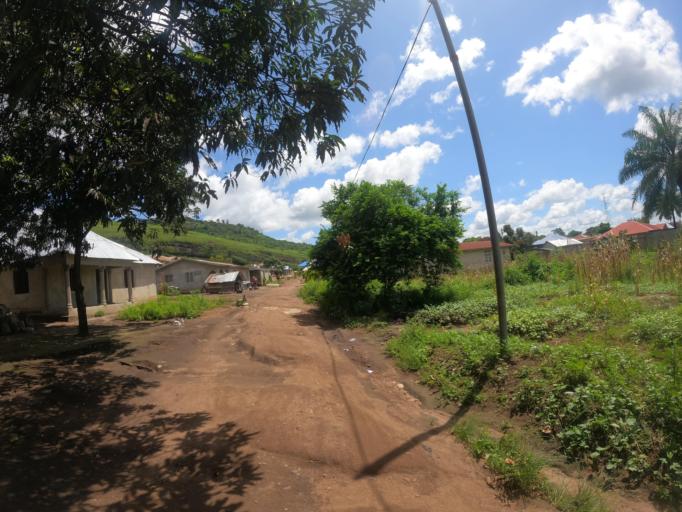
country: SL
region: Northern Province
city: Makeni
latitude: 8.8869
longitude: -12.0662
